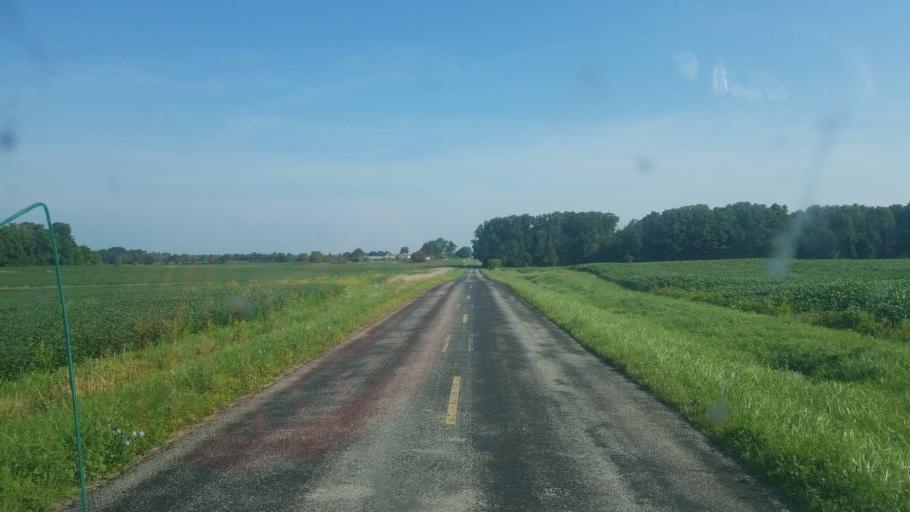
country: US
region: Ohio
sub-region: Huron County
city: New London
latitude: 41.0675
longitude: -82.3467
